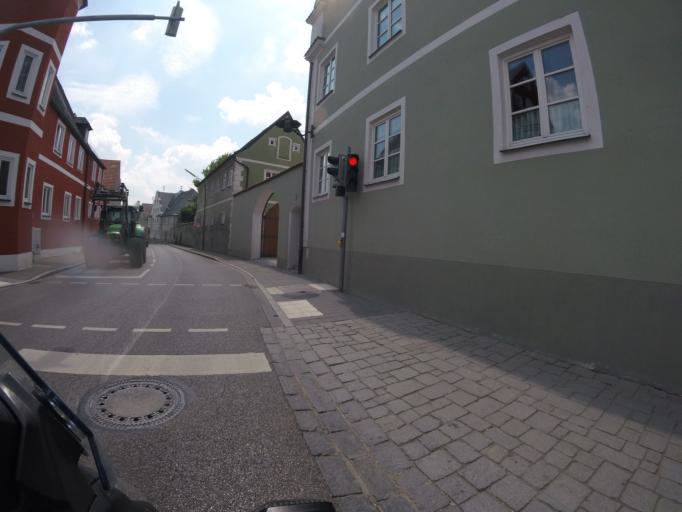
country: DE
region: Bavaria
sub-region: Upper Bavaria
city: Geisenfeld
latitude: 48.6835
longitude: 11.6115
